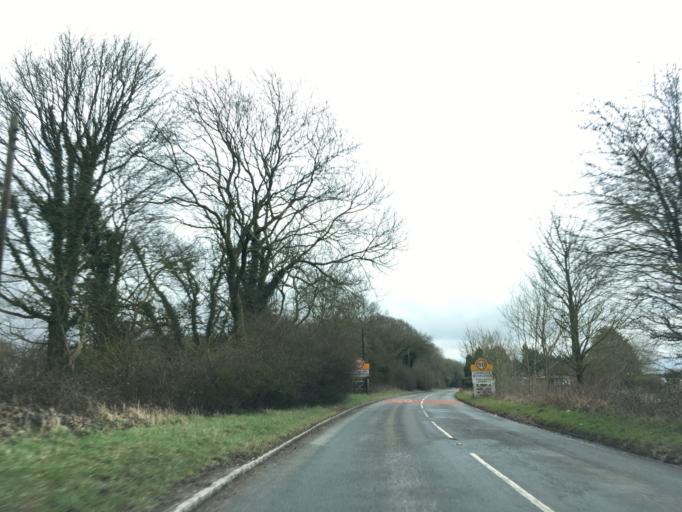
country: GB
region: England
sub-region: West Berkshire
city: Lambourn
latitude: 51.4885
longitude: -1.5637
